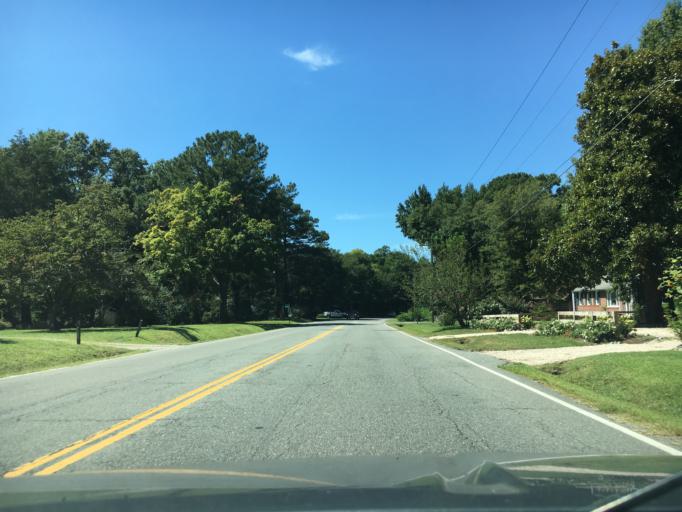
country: US
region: Virginia
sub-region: Henrico County
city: Tuckahoe
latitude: 37.5977
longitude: -77.5404
